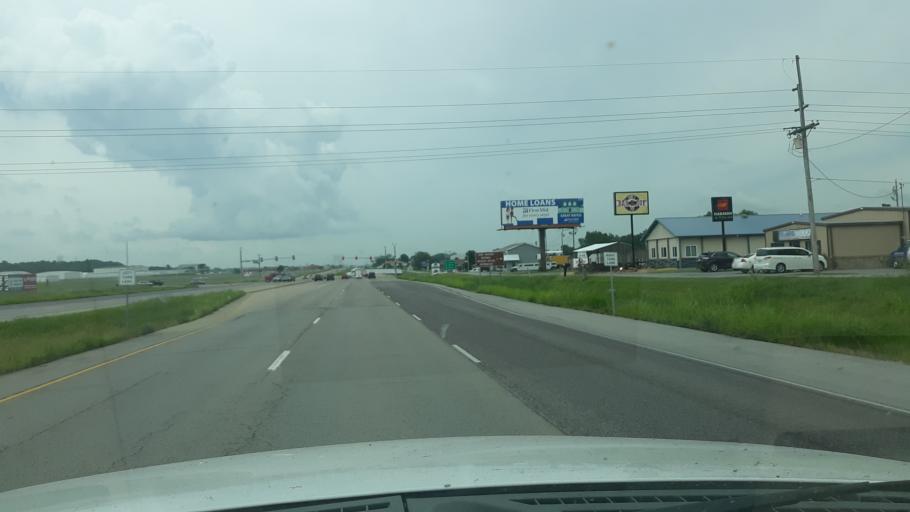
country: US
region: Illinois
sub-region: Williamson County
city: Energy
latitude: 37.7450
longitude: -89.0239
